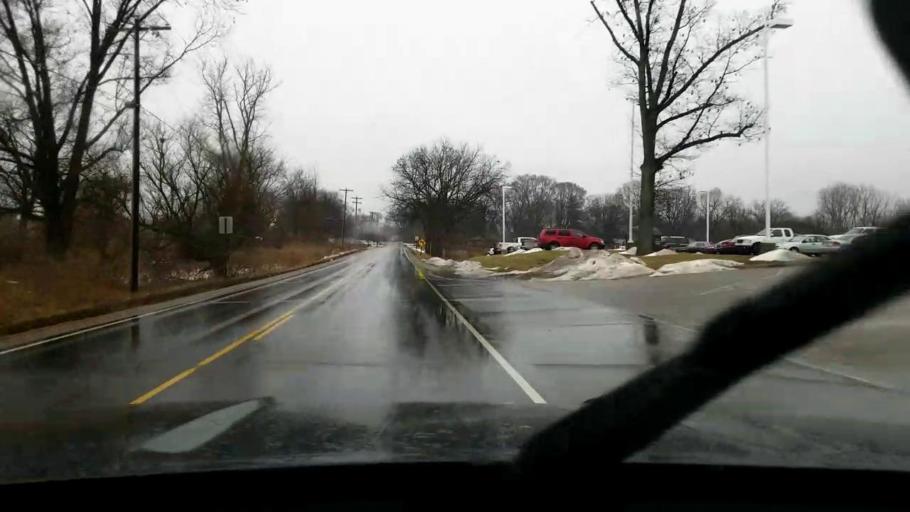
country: US
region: Michigan
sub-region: Jackson County
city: Jackson
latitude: 42.2778
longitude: -84.3736
